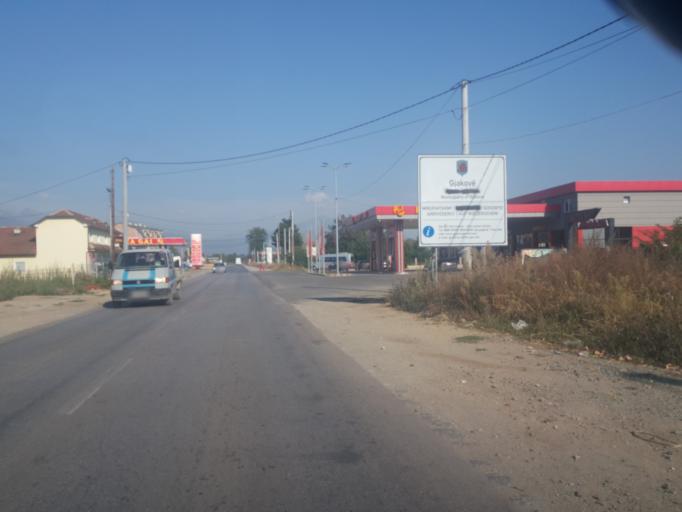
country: XK
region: Gjakova
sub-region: Komuna e Gjakoves
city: Gjakove
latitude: 42.4085
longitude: 20.4060
